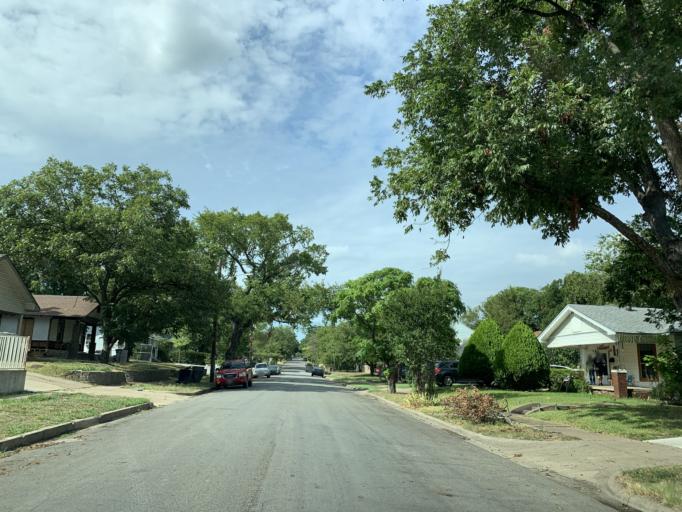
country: US
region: Texas
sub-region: Dallas County
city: Cockrell Hill
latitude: 32.7362
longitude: -96.8504
